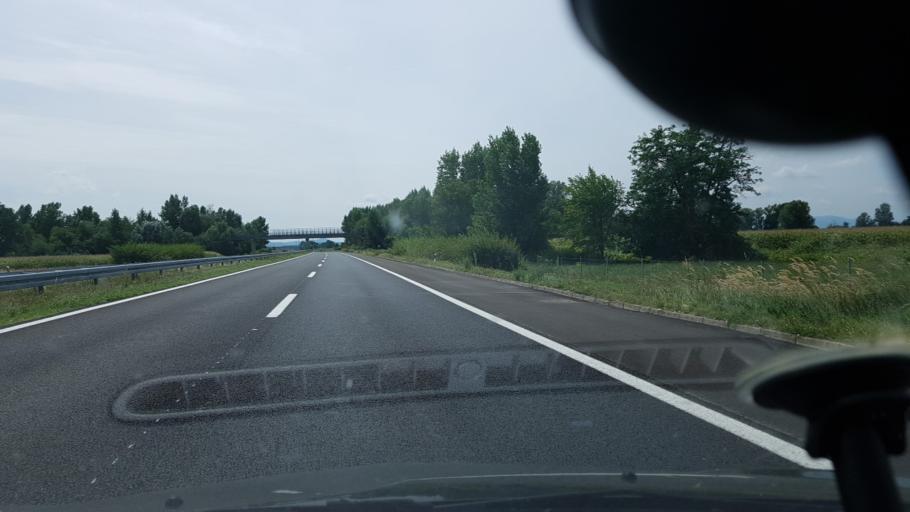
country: HR
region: Medimurska
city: Mala Subotica
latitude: 46.3594
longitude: 16.5384
